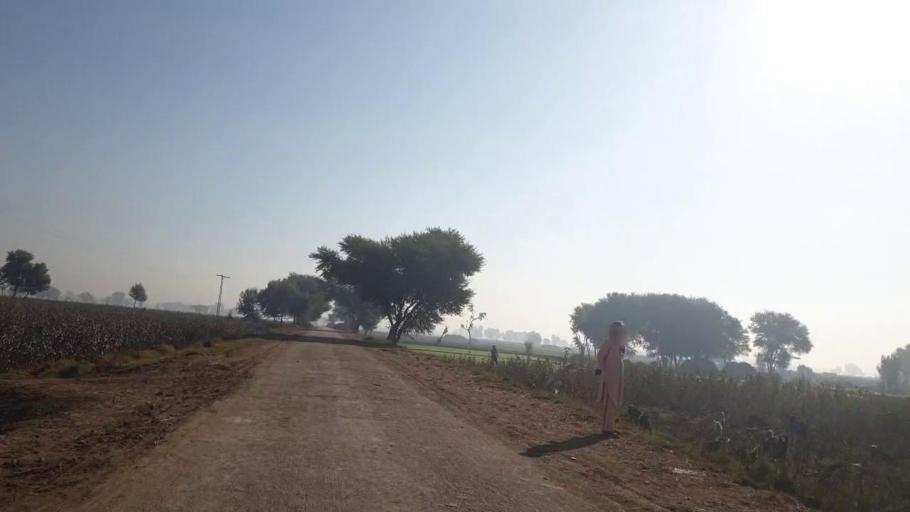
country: PK
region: Sindh
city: Dadu
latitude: 26.6761
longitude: 67.7825
